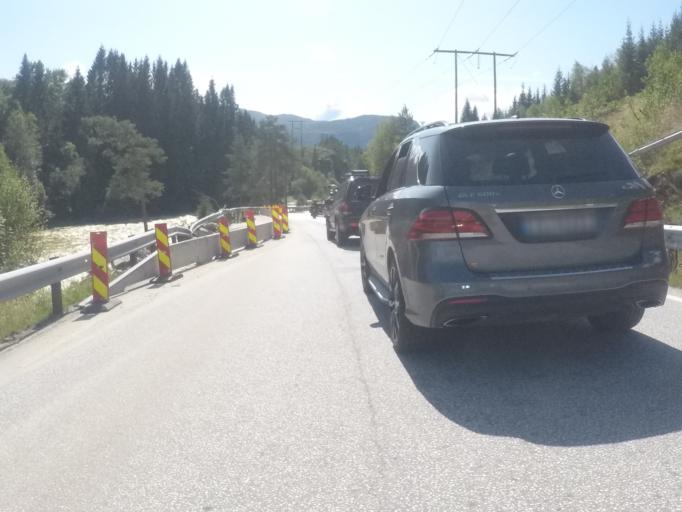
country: NO
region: Sogn og Fjordane
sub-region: Forde
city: Forde
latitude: 61.4559
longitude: 6.0142
